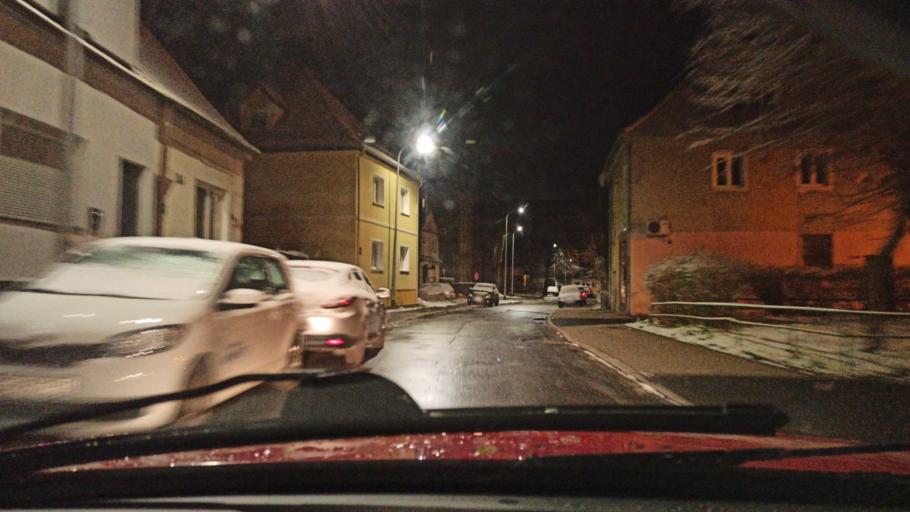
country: PL
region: Warmian-Masurian Voivodeship
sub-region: Powiat elblaski
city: Elblag
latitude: 54.1719
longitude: 19.4105
